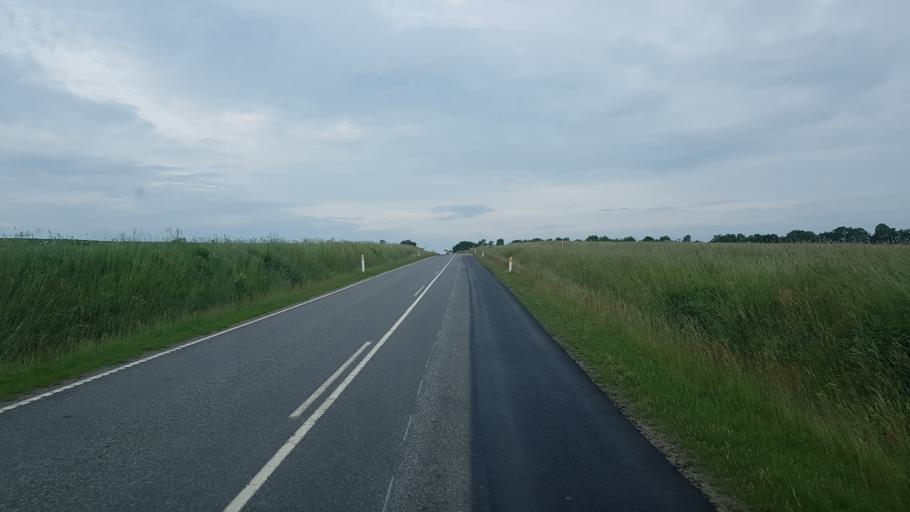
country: DK
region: South Denmark
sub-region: Vejen Kommune
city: Holsted
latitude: 55.4415
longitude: 8.9468
